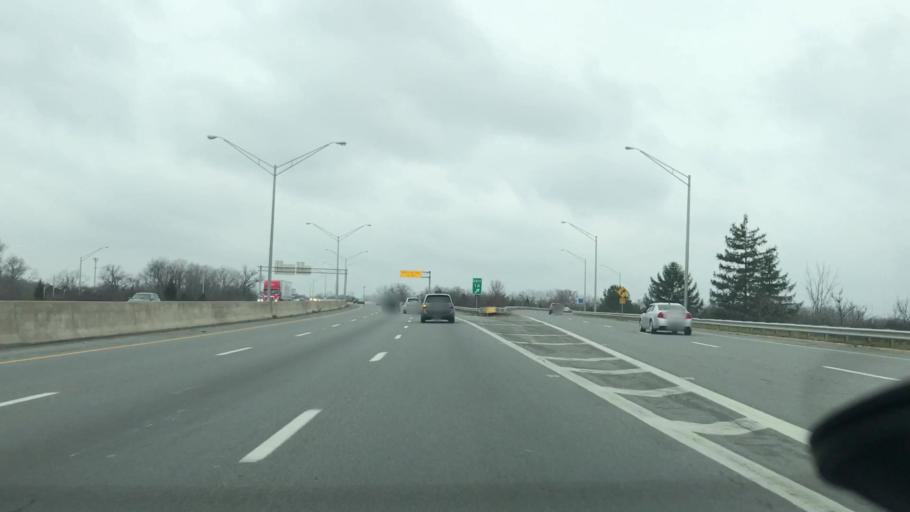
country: US
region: Ohio
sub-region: Franklin County
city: Grandview Heights
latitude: 39.9690
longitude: -83.0529
